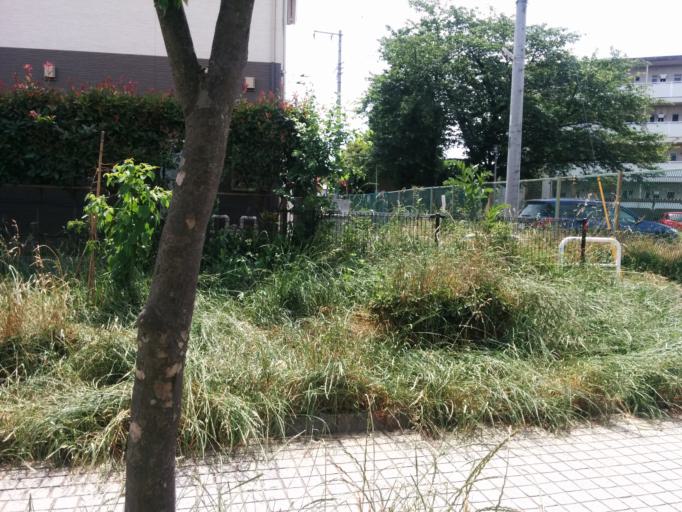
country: JP
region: Tokyo
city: Higashimurayama-shi
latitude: 35.7680
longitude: 139.4901
